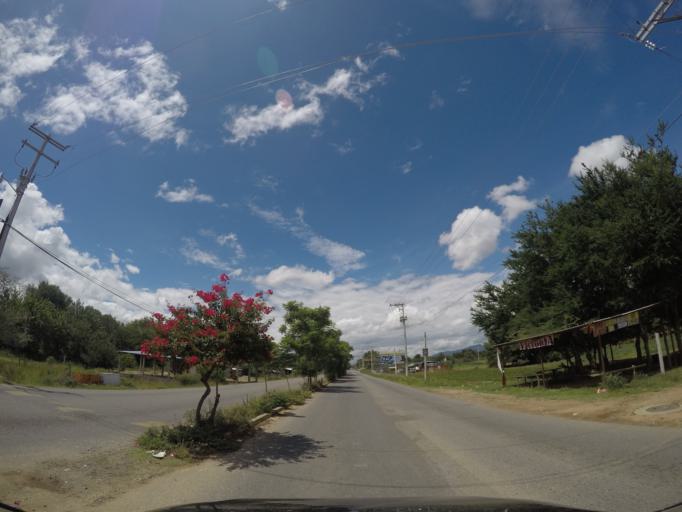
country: MX
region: Oaxaca
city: San Raymundo Jalpam
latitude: 16.9738
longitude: -96.7503
